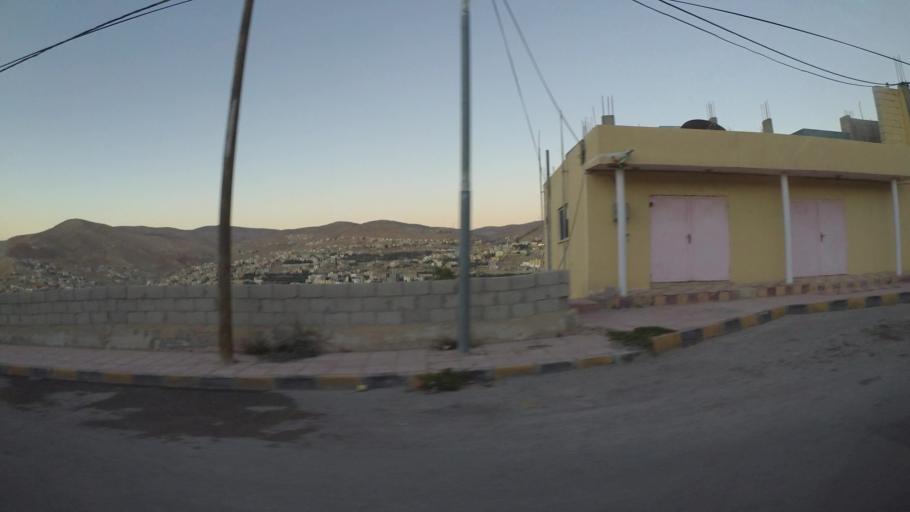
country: JO
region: Ma'an
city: Petra
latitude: 30.3171
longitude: 35.4750
